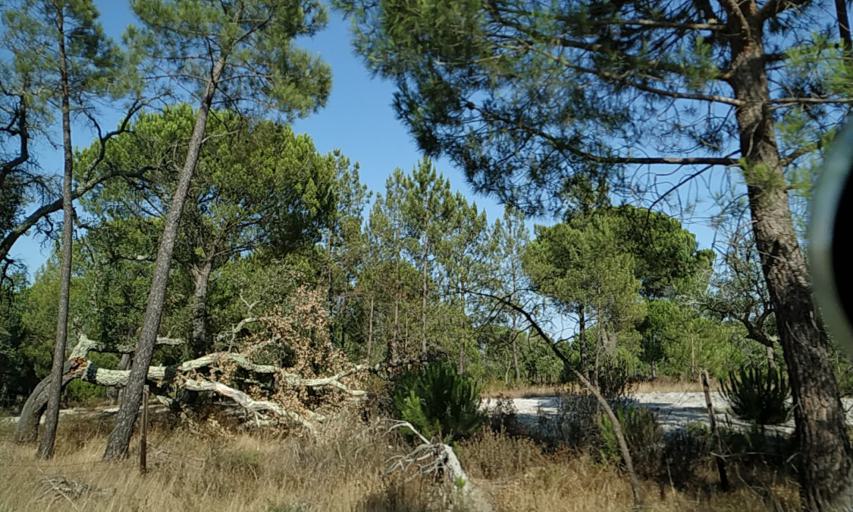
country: PT
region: Santarem
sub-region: Coruche
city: Coruche
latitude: 38.9055
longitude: -8.5274
